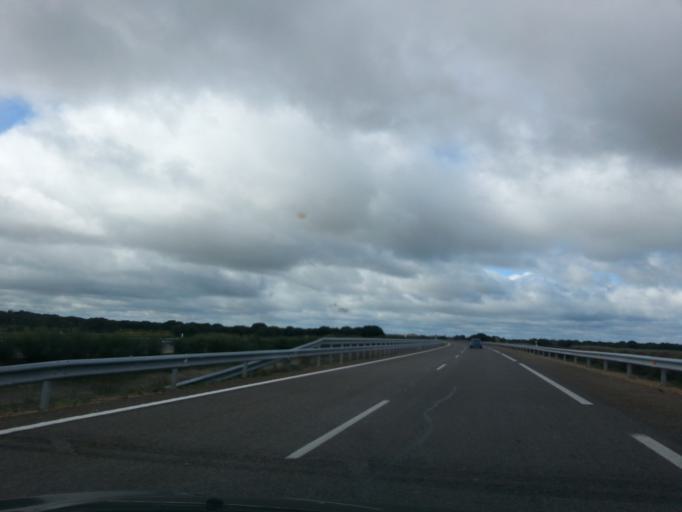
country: ES
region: Castille and Leon
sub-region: Provincia de Salamanca
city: Cabrillas
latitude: 40.8060
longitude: -6.1912
